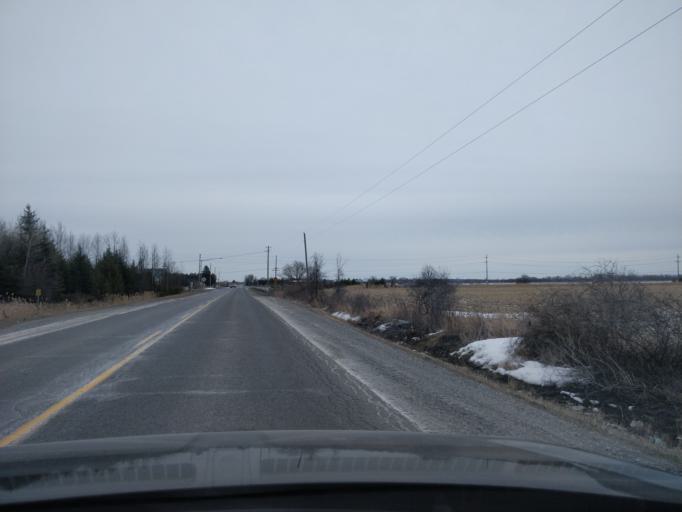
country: CA
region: Ontario
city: Bells Corners
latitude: 45.2466
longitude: -75.8881
